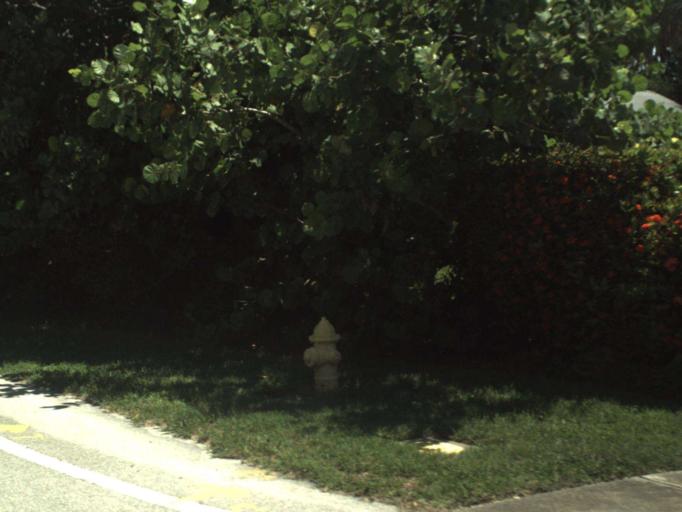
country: US
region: Florida
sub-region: Indian River County
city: Vero Beach
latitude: 27.6516
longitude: -80.3604
